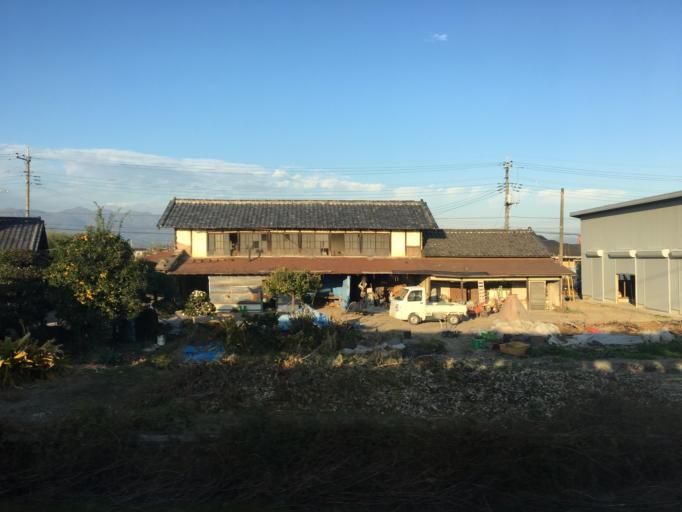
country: JP
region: Gunma
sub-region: Sawa-gun
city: Tamamura
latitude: 36.3591
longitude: 139.1302
